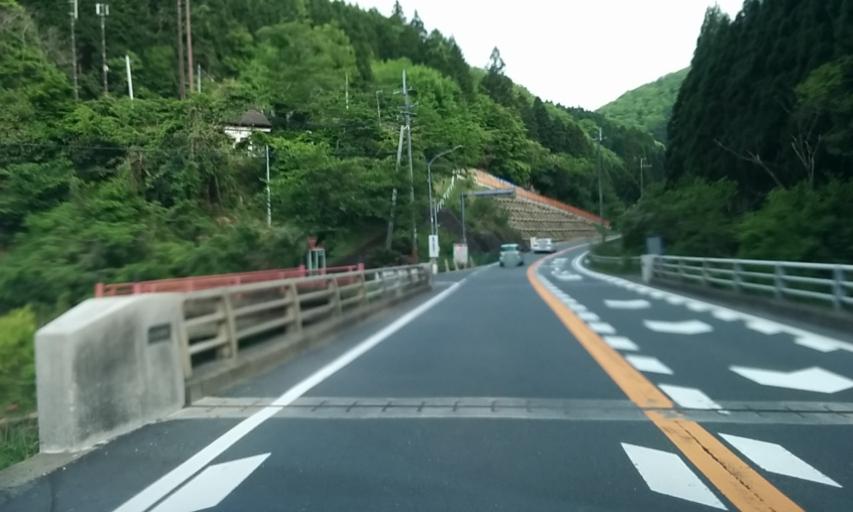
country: JP
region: Kyoto
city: Ayabe
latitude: 35.2449
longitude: 135.2939
